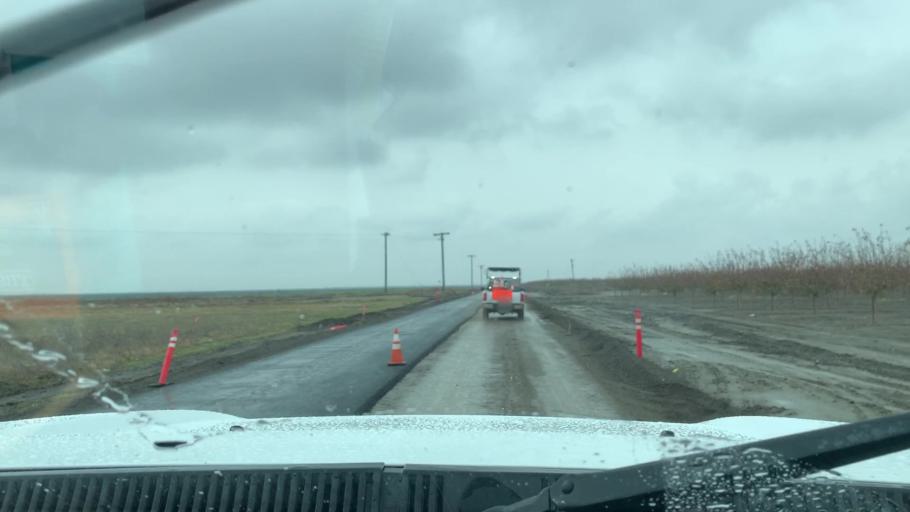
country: US
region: California
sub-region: Kings County
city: Corcoran
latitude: 36.0073
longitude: -119.5061
